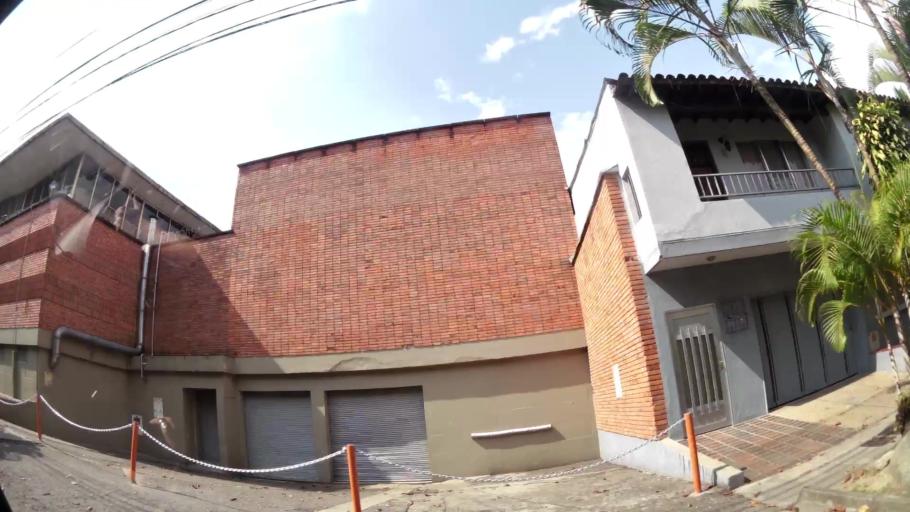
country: CO
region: Antioquia
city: Medellin
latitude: 6.2376
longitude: -75.5863
